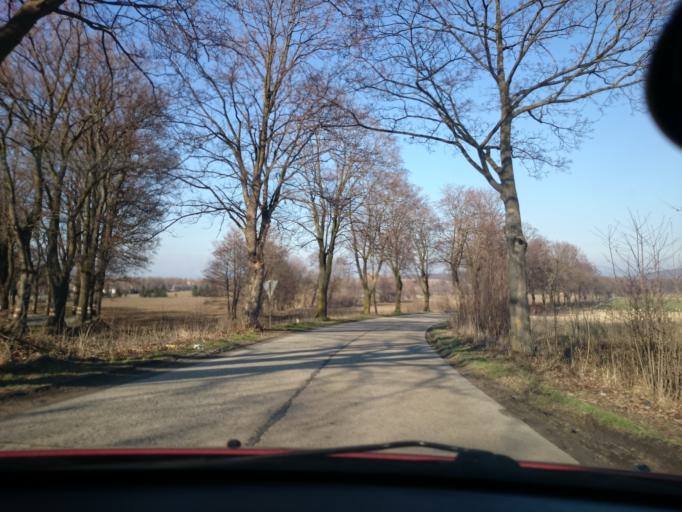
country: PL
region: Lower Silesian Voivodeship
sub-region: Powiat klodzki
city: Bystrzyca Klodzka
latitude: 50.3449
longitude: 16.5928
